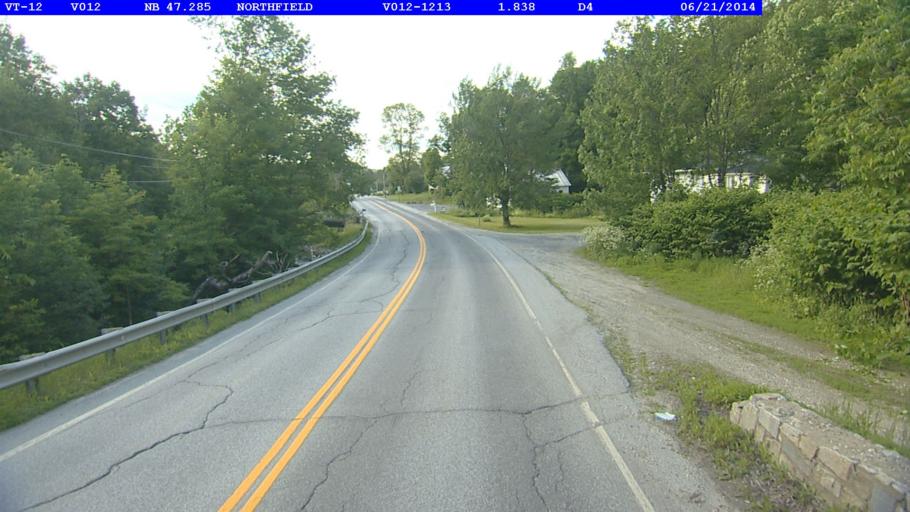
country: US
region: Vermont
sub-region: Washington County
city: Northfield
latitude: 44.1159
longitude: -72.6545
